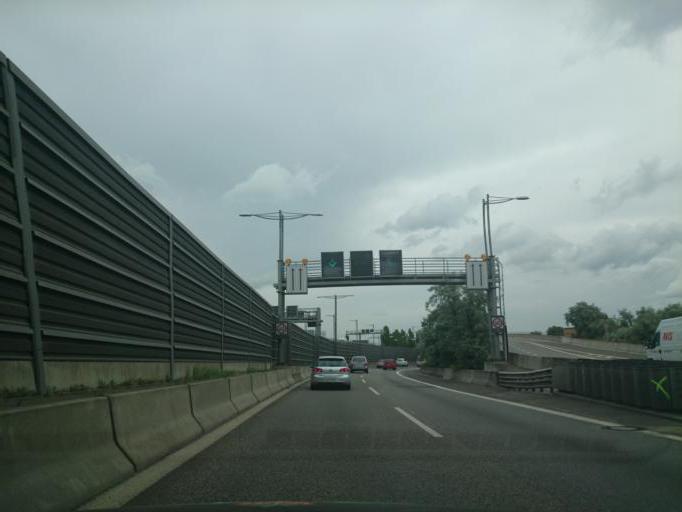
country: DE
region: Berlin
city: Treptow Bezirk
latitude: 52.4637
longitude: 13.4505
